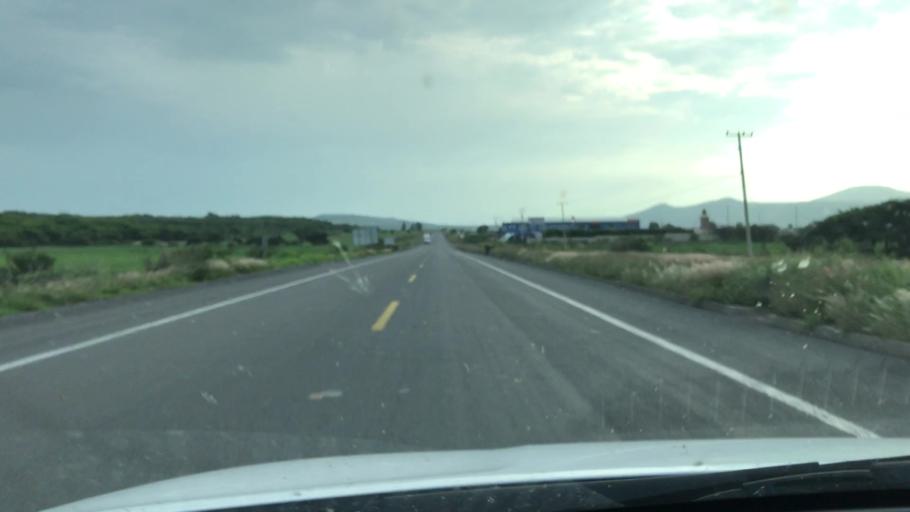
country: MX
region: Jalisco
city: Degollado
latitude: 20.3646
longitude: -102.1377
